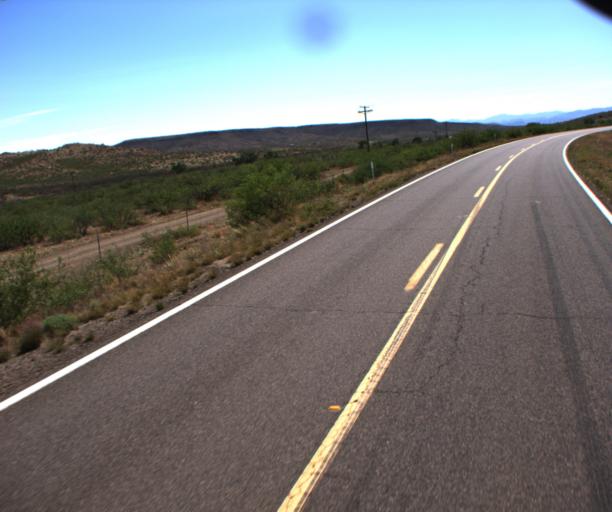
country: US
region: Arizona
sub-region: Cochise County
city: Douglas
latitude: 31.4859
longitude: -109.4153
